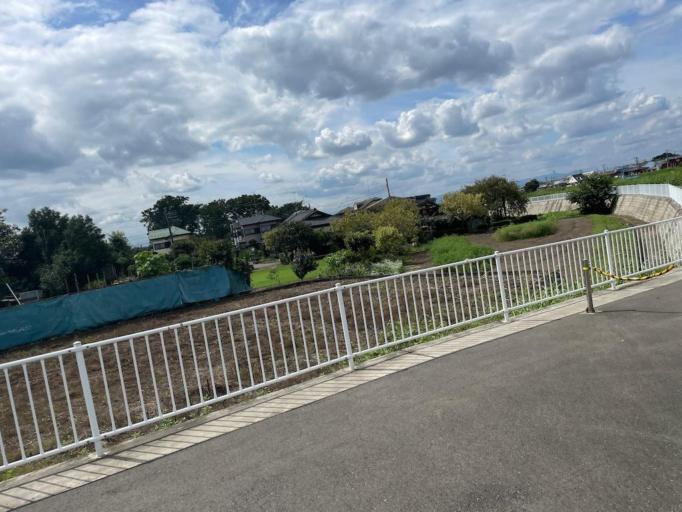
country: JP
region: Saitama
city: Kamifukuoka
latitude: 35.8901
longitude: 139.5215
